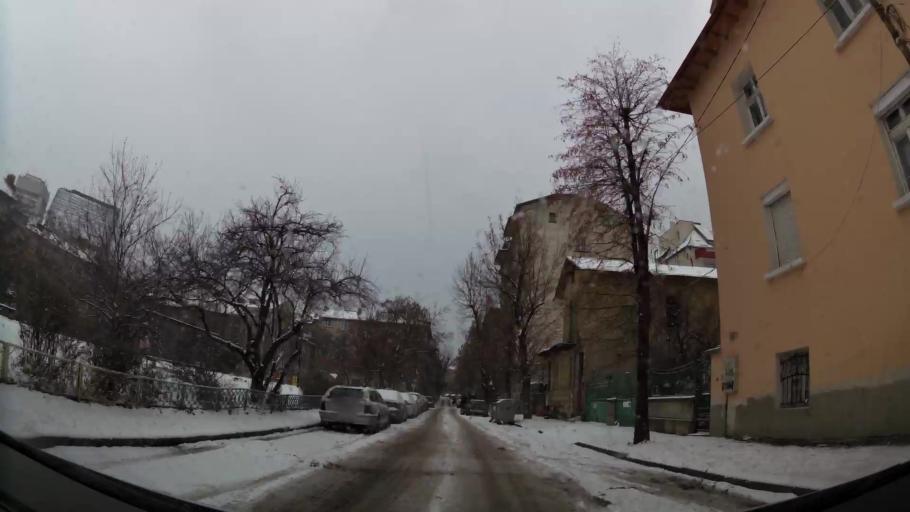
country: BG
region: Sofia-Capital
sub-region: Stolichna Obshtina
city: Sofia
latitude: 42.6954
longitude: 23.3127
